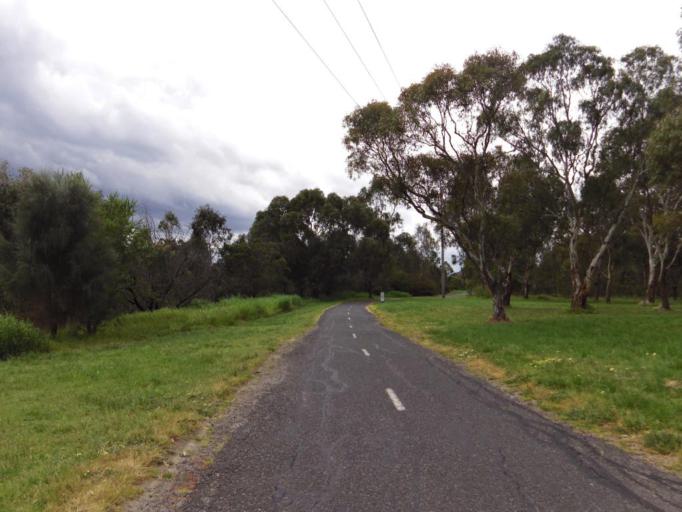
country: AU
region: Victoria
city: Abbotsford
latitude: -37.7918
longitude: 145.0064
